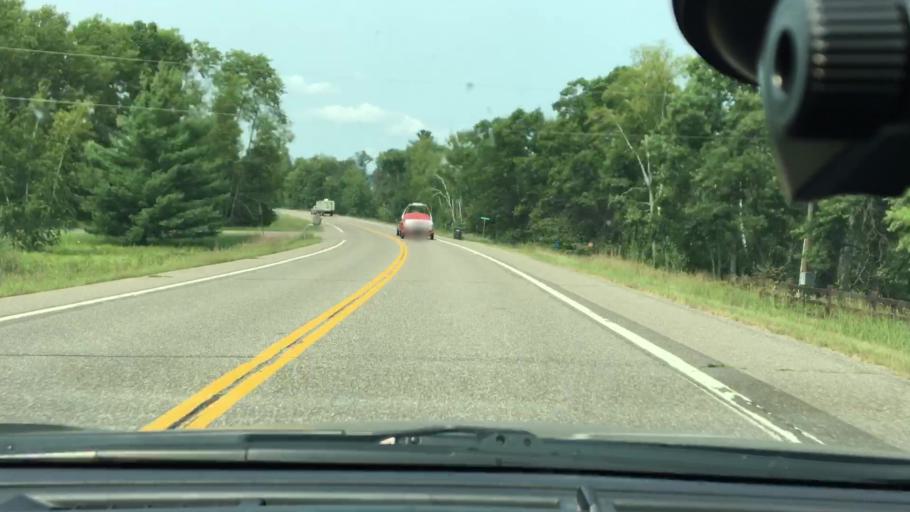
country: US
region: Minnesota
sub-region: Cass County
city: East Gull Lake
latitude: 46.4012
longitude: -94.3506
